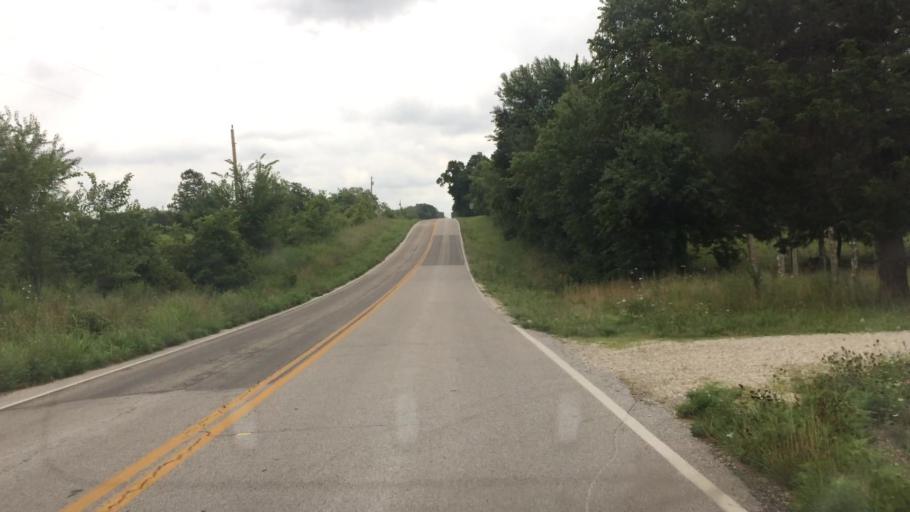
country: US
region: Missouri
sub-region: Webster County
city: Marshfield
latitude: 37.3416
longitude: -93.0188
